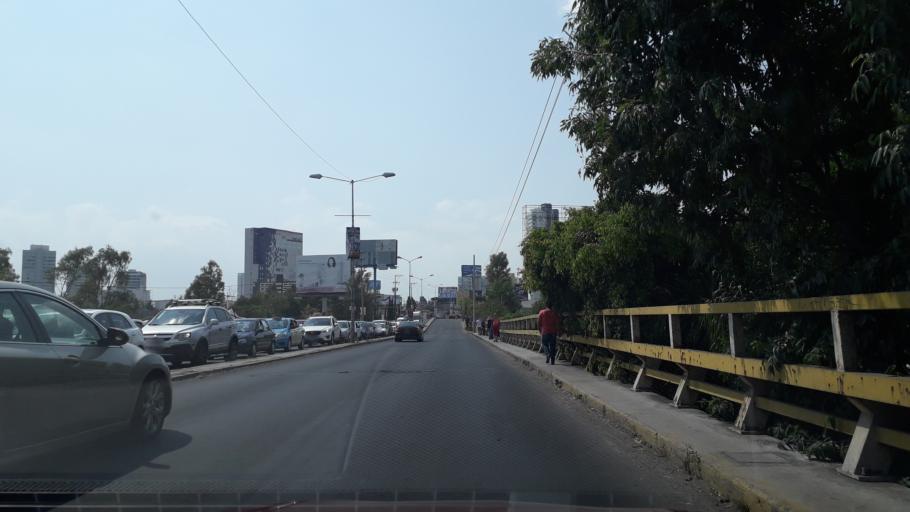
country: MX
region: Puebla
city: Puebla
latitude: 19.0256
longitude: -98.2240
